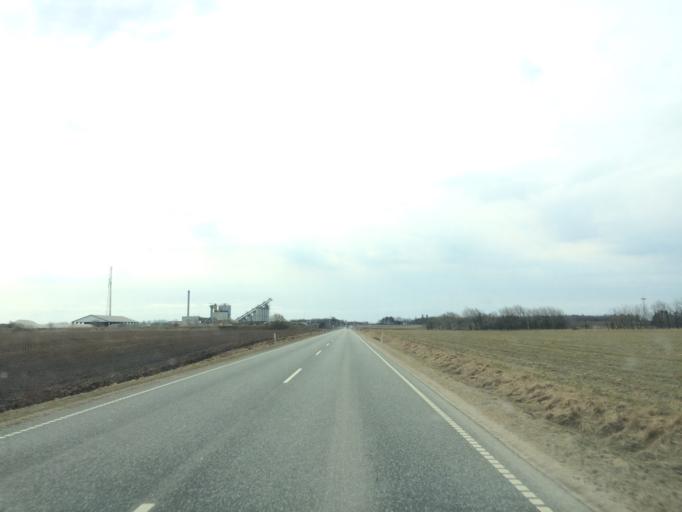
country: DK
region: Central Jutland
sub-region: Ringkobing-Skjern Kommune
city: Videbaek
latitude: 56.0956
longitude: 8.5075
